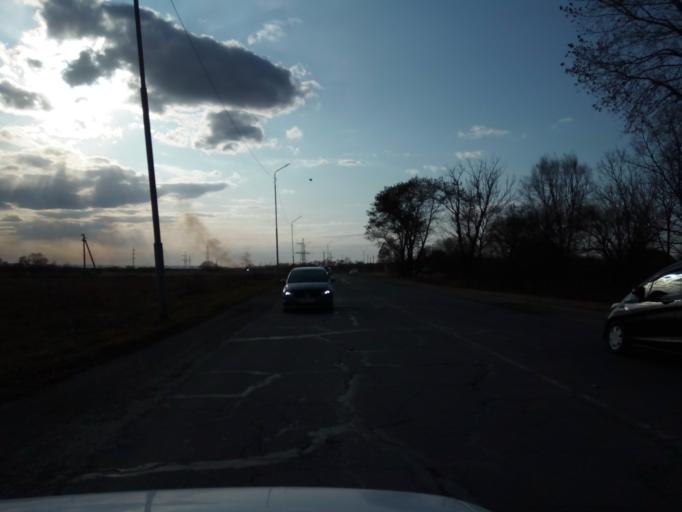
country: RU
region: Primorskiy
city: Dal'nerechensk
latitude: 45.9171
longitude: 133.7675
